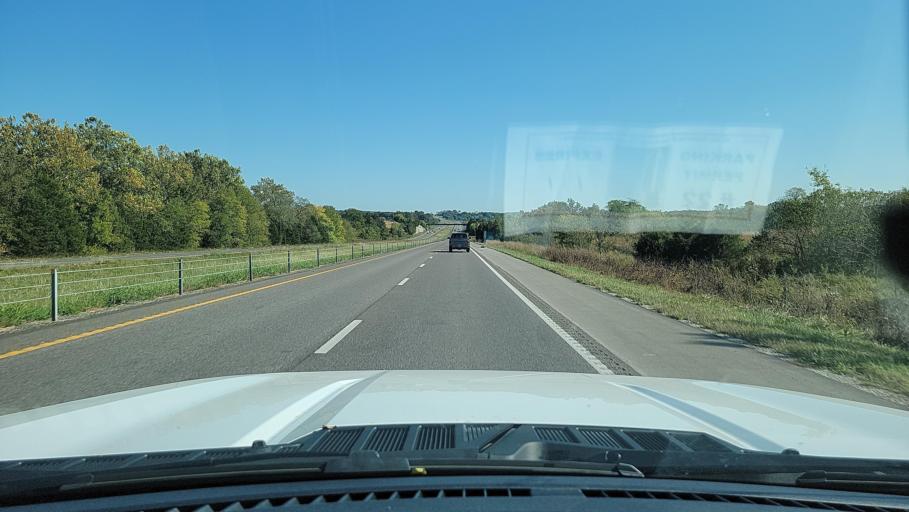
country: US
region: Missouri
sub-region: Sainte Genevieve County
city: Sainte Genevieve
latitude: 37.9545
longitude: -90.1549
